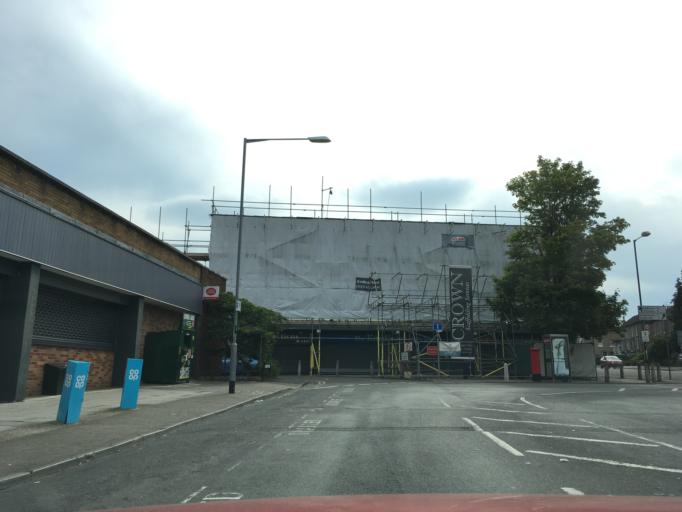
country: GB
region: England
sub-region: South Gloucestershire
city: Mangotsfield
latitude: 51.4819
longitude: -2.5255
